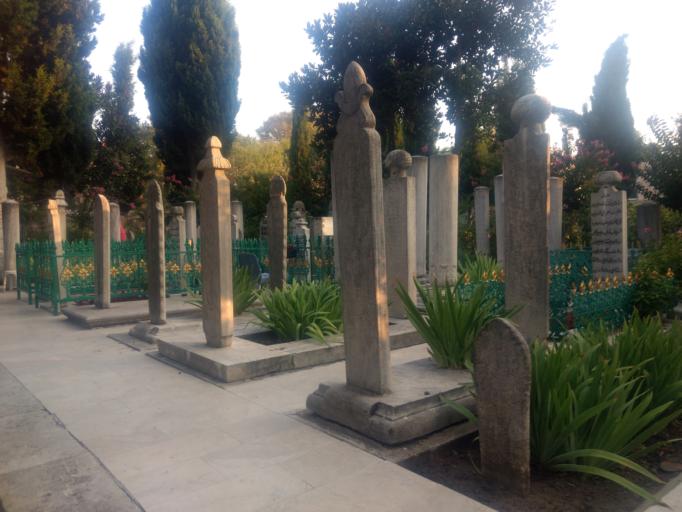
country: TR
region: Istanbul
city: Eminoenue
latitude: 41.0156
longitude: 28.9645
